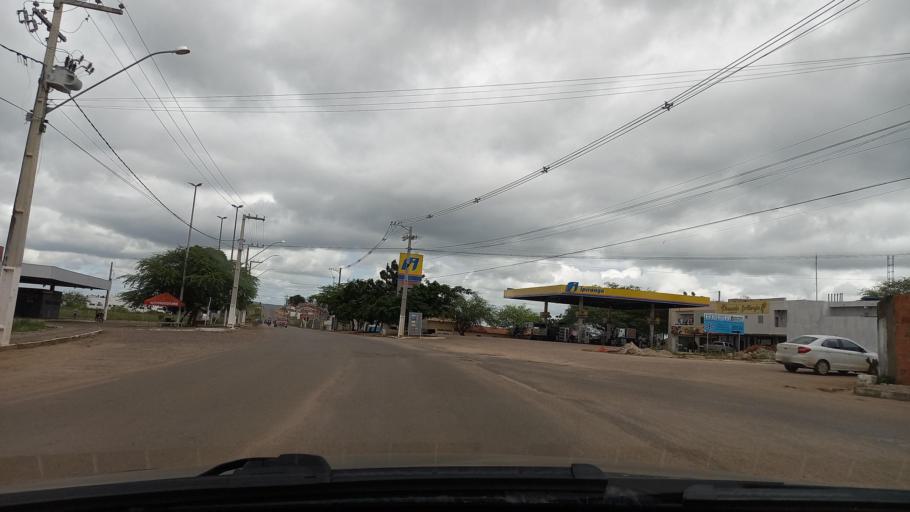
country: BR
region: Sergipe
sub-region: Caninde De Sao Francisco
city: Caninde de Sao Francisco
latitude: -9.6671
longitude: -37.7962
